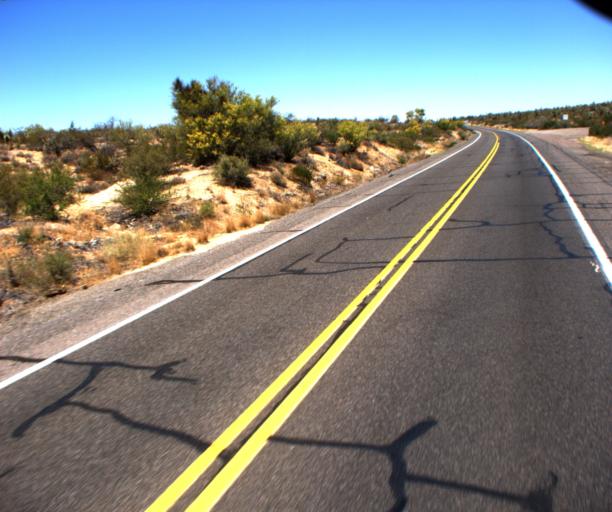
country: US
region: Arizona
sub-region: Yavapai County
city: Congress
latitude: 34.2299
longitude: -113.0703
